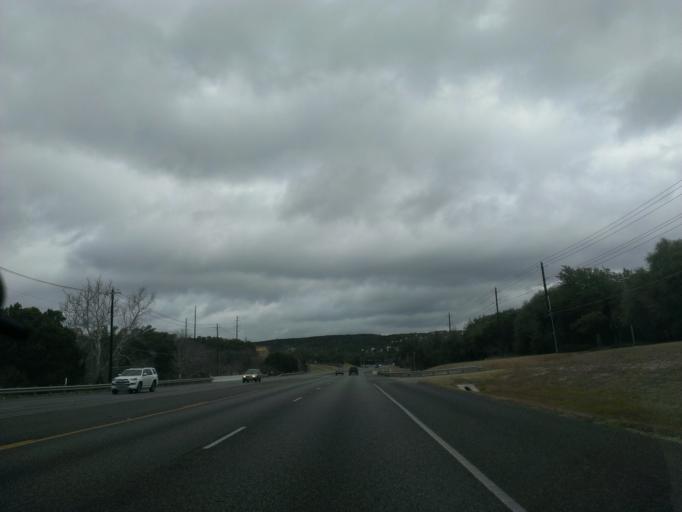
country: US
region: Texas
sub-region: Travis County
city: West Lake Hills
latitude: 30.3723
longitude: -97.8036
